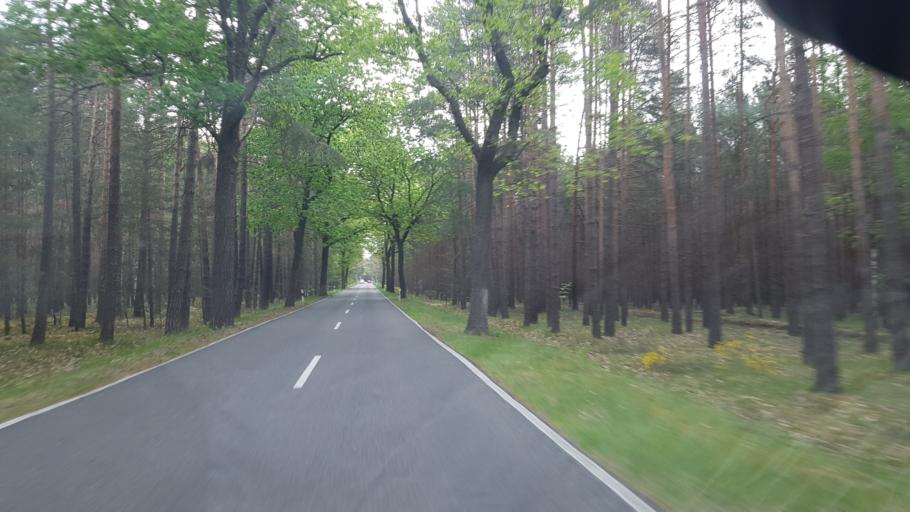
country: DE
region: Brandenburg
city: Baruth
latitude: 51.9784
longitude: 13.4625
